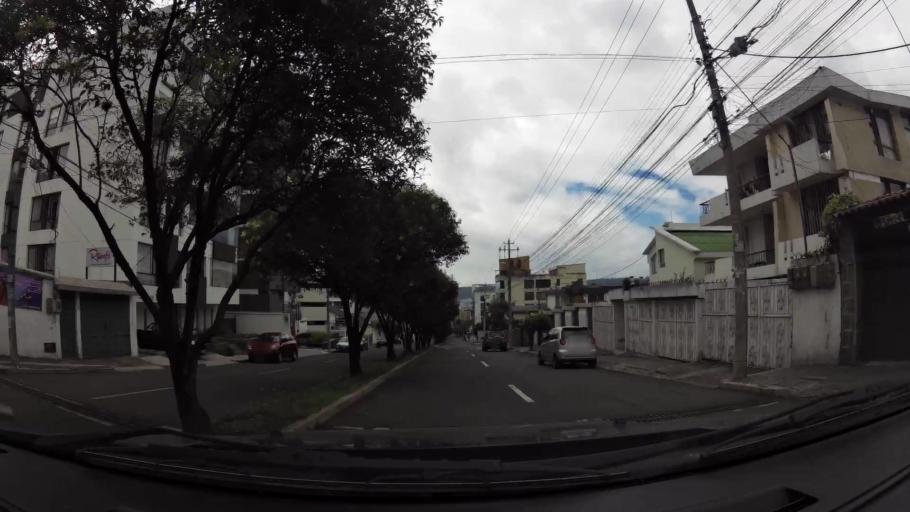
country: EC
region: Pichincha
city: Quito
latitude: -0.1710
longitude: -78.4966
